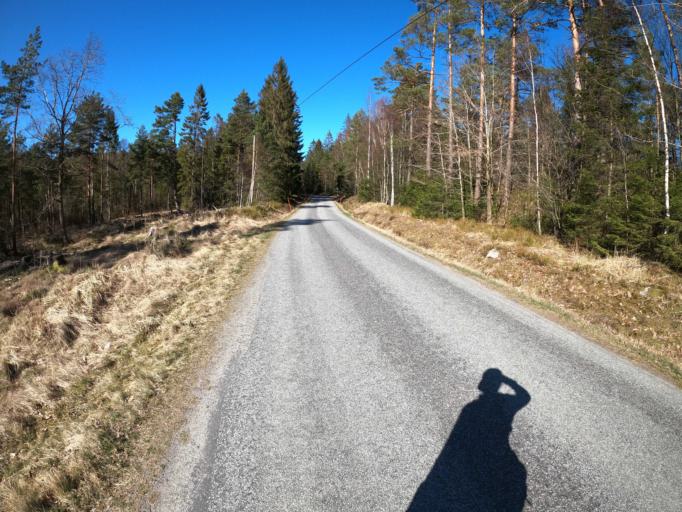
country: SE
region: Vaestra Goetaland
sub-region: Harryda Kommun
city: Molnlycke
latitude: 57.6374
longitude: 12.1134
